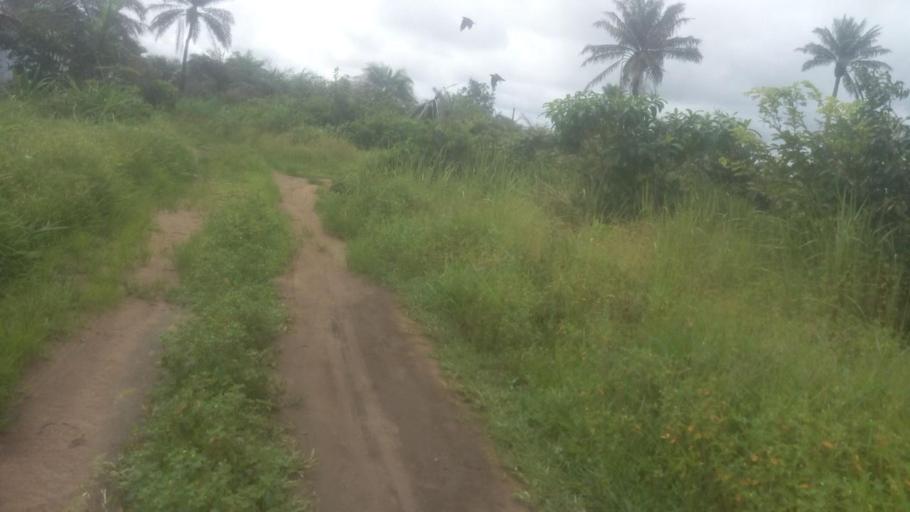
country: SL
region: Northern Province
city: Masoyila
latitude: 8.5899
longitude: -13.1845
